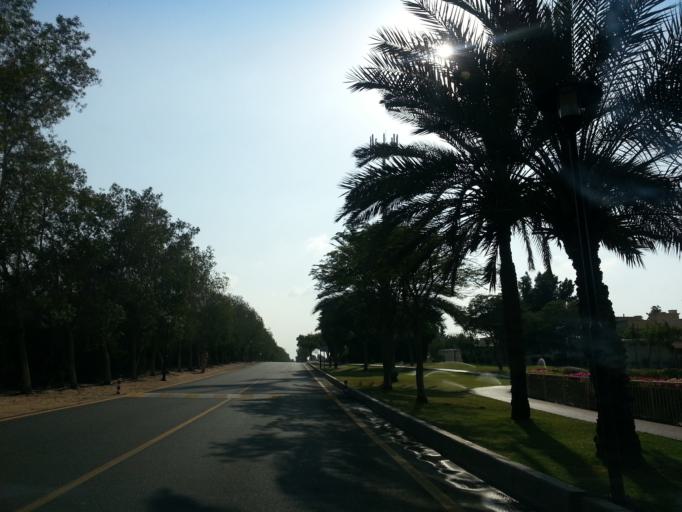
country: AE
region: Dubai
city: Dubai
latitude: 25.0585
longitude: 55.1889
